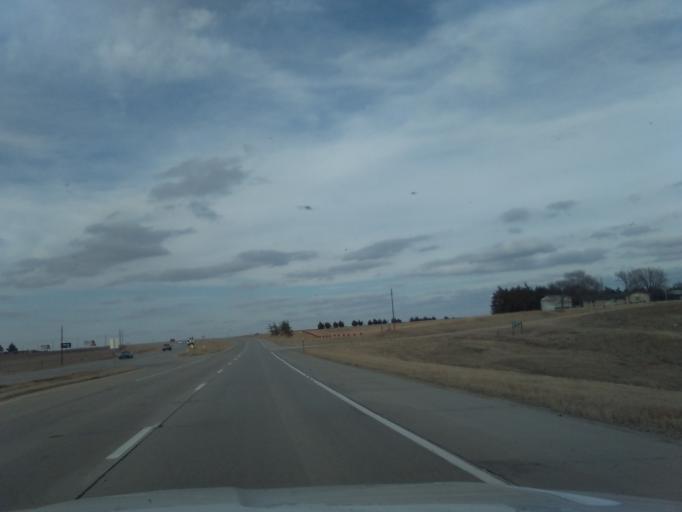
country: US
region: Nebraska
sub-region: Gage County
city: Beatrice
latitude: 40.3487
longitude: -96.7451
